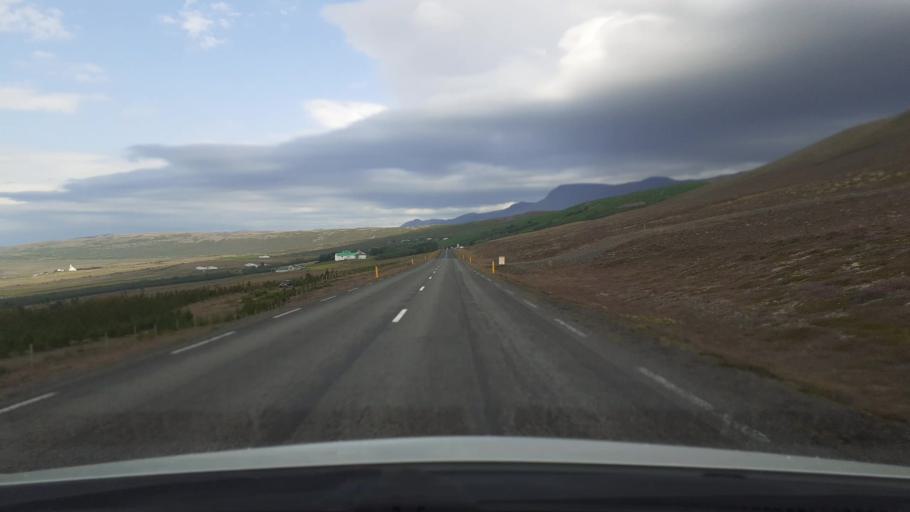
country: IS
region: Capital Region
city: Mosfellsbaer
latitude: 64.4065
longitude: -21.5793
